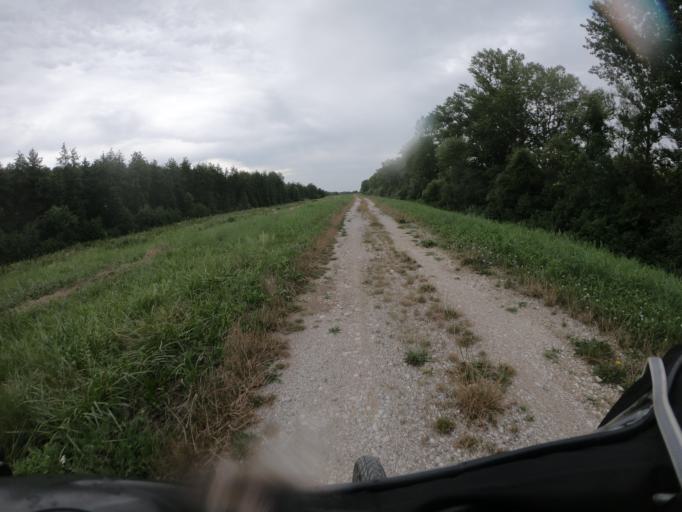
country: HU
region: Jasz-Nagykun-Szolnok
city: Tiszafured
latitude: 47.6814
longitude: 20.7750
